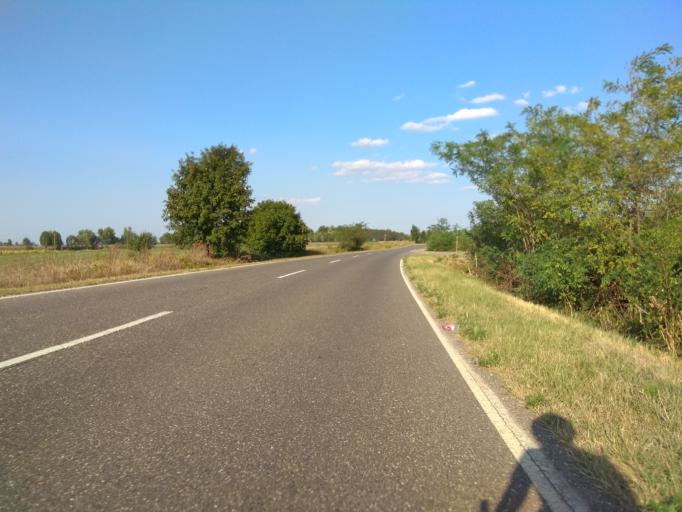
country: HU
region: Borsod-Abauj-Zemplen
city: Onod
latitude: 47.9757
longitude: 20.9031
